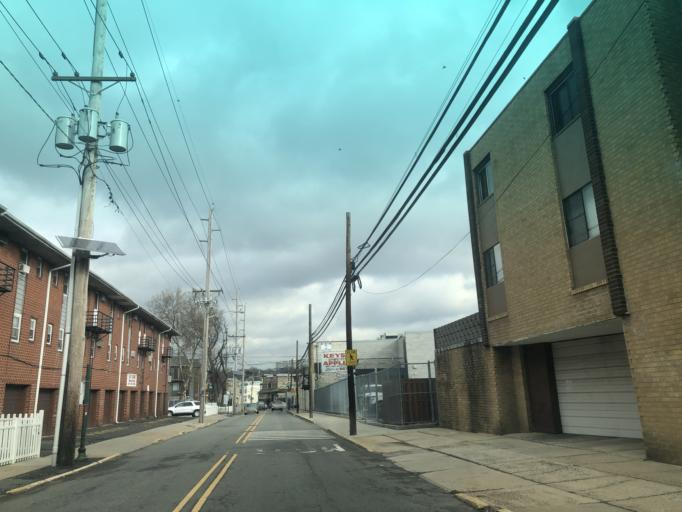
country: US
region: New Jersey
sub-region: Hudson County
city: Union City
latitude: 40.7817
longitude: -74.0342
